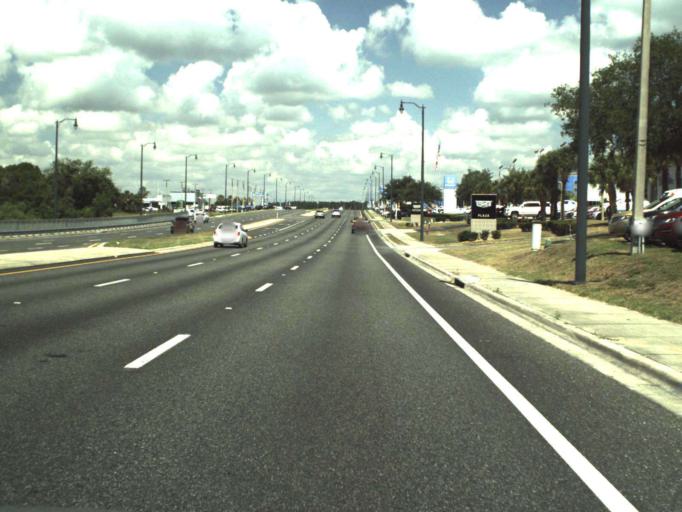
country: US
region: Florida
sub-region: Lake County
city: Silver Lake
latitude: 28.8298
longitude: -81.8087
